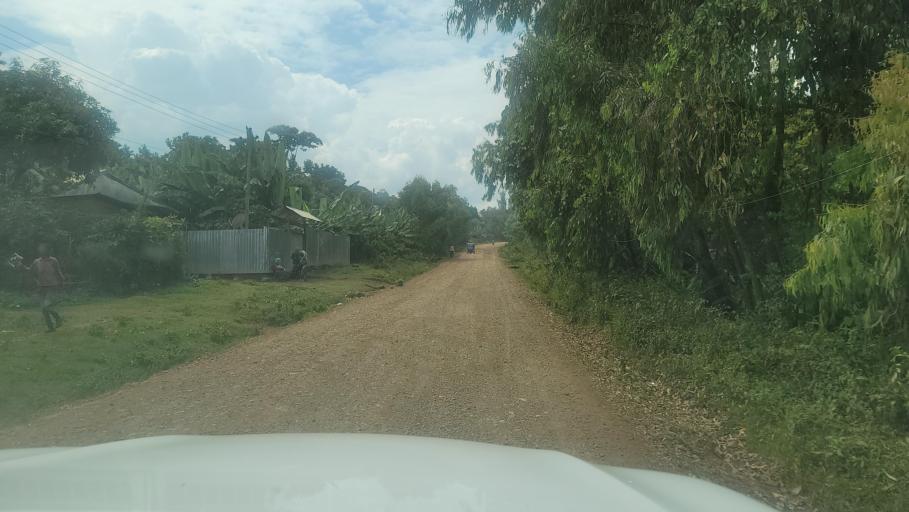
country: ET
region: Oromiya
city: Agaro
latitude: 7.8314
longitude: 36.5432
